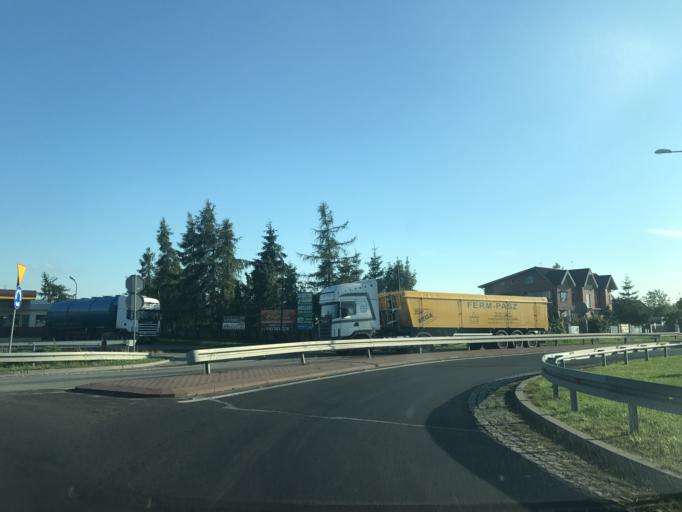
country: PL
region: Greater Poland Voivodeship
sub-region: Powiat koninski
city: Rychwal
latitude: 52.0677
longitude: 18.1619
